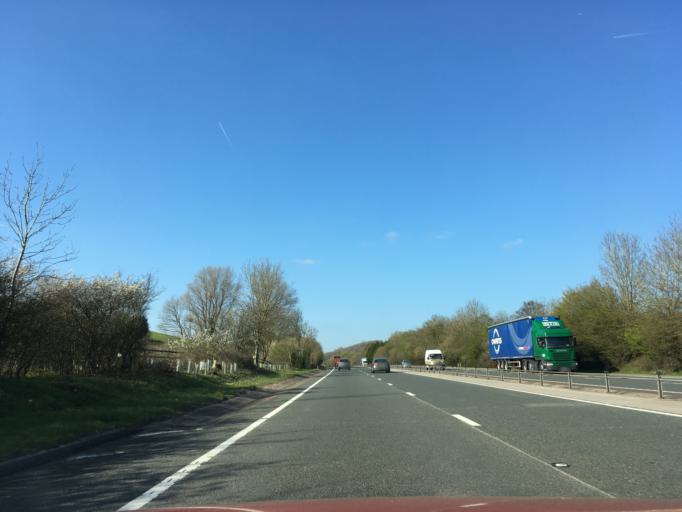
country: GB
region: Wales
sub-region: Monmouthshire
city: Llangybi
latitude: 51.6746
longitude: -2.8768
